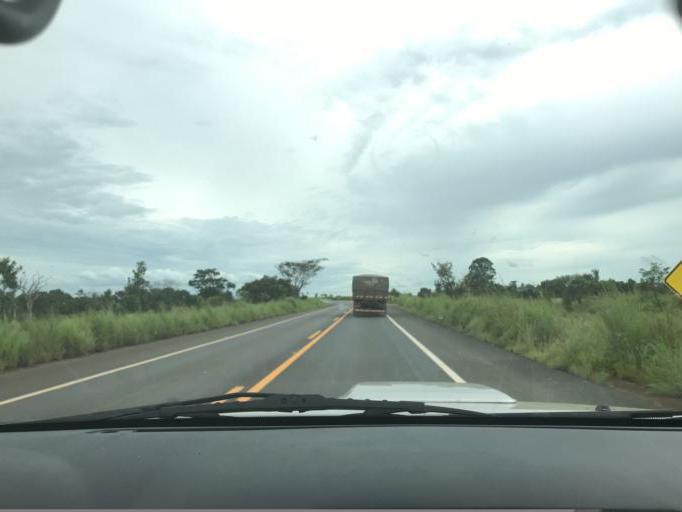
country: BR
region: Minas Gerais
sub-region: Araxa
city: Araxa
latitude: -19.3819
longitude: -46.8597
